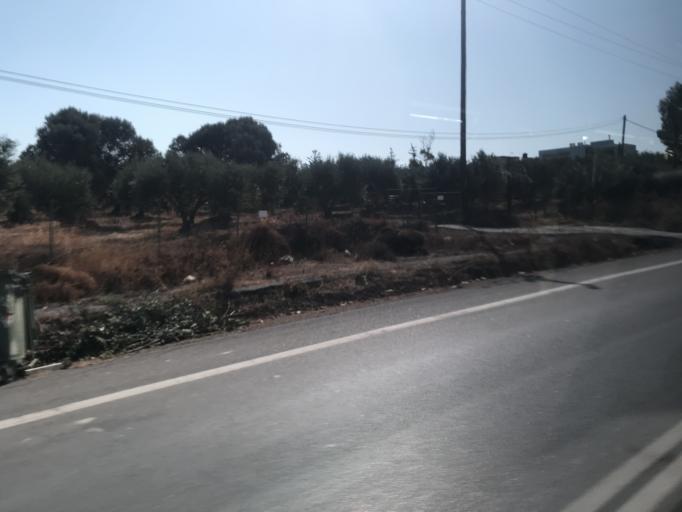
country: GR
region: Crete
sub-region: Nomos Irakleiou
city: Gazi
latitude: 35.3098
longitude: 25.0909
